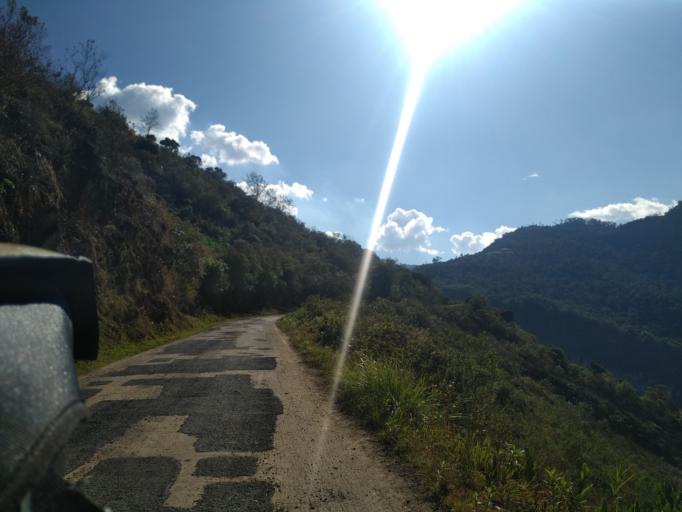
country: PE
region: Amazonas
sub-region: Provincia de Chachapoyas
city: Montevideo
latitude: -6.7147
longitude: -77.8158
